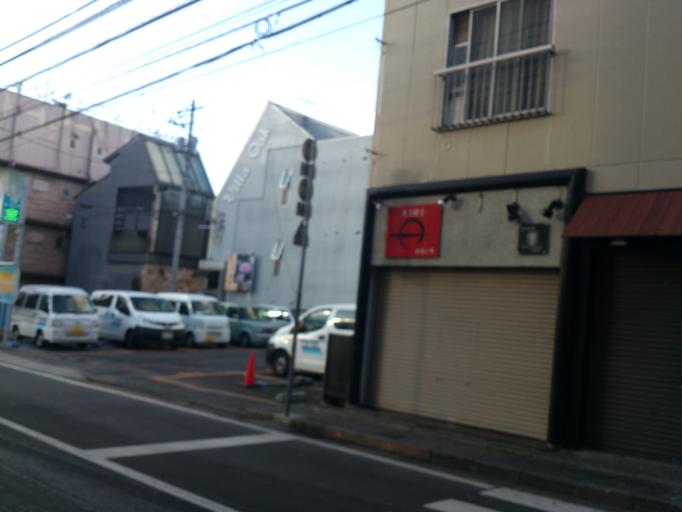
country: JP
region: Ibaraki
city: Mito-shi
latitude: 36.3815
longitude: 140.4592
